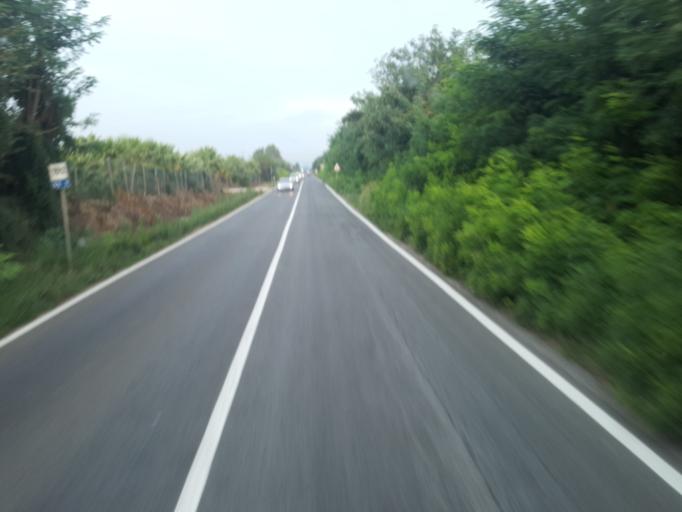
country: IT
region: Campania
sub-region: Provincia di Caserta
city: Pignataro Maggiore
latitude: 41.1689
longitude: 14.1487
